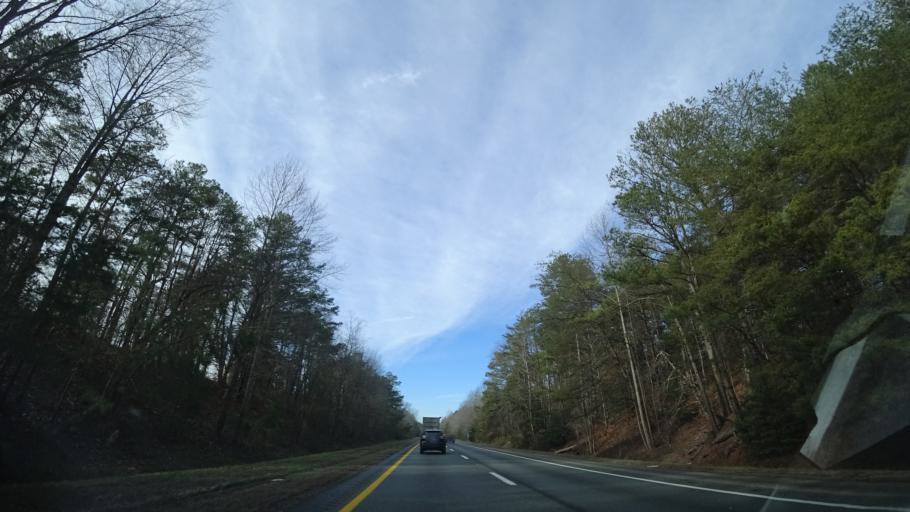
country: US
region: Virginia
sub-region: New Kent County
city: New Kent
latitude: 37.4895
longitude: -76.9888
